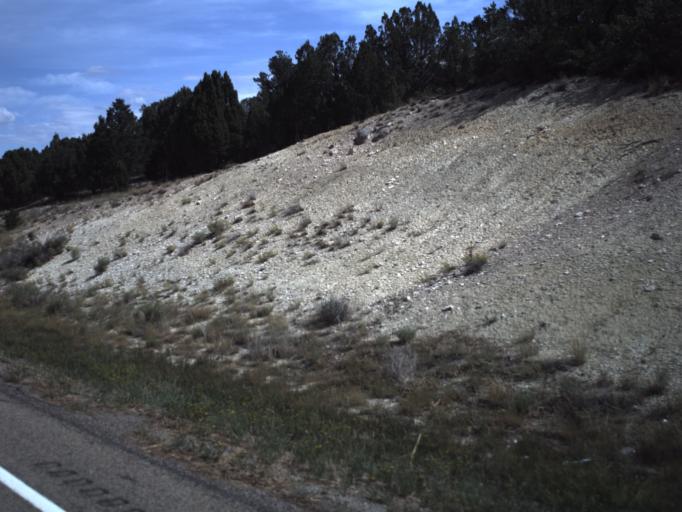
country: US
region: Utah
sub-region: Sanpete County
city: Fairview
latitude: 39.7438
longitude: -111.4773
